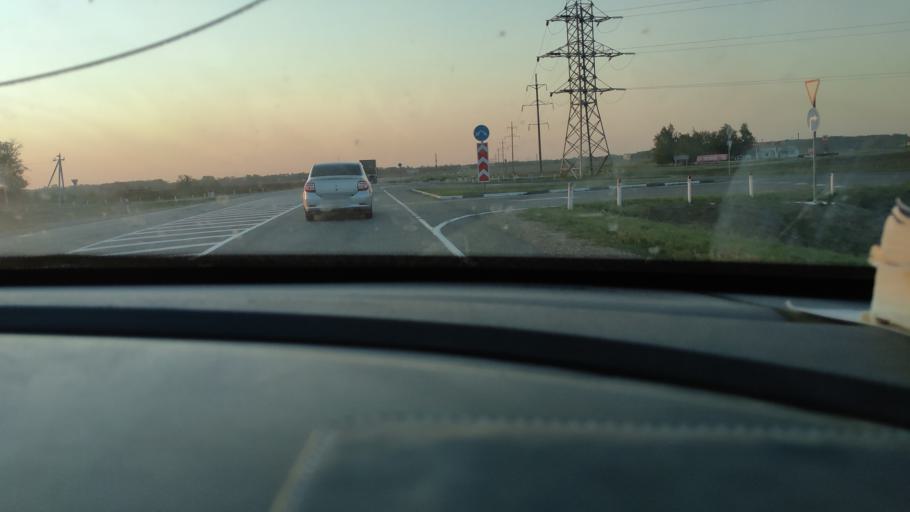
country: RU
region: Krasnodarskiy
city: Starominskaya
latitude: 46.5021
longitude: 39.0406
